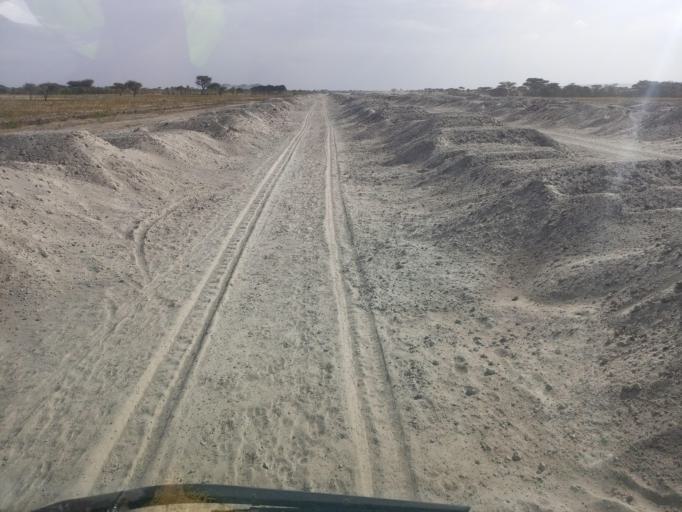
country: ET
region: Oromiya
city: Ziway
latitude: 7.8781
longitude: 38.6731
